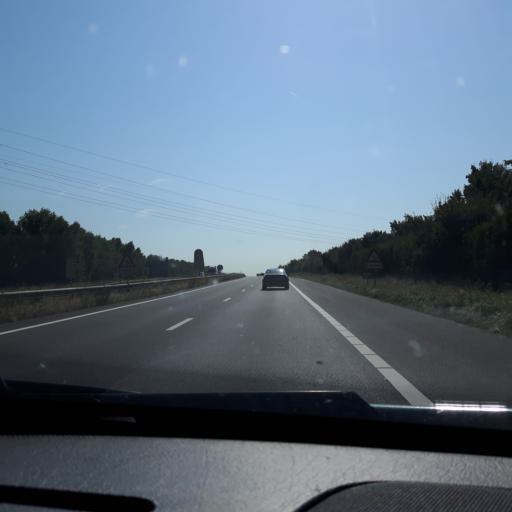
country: NL
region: Zeeland
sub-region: Gemeente Goes
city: Goes
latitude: 51.5003
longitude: 3.8711
